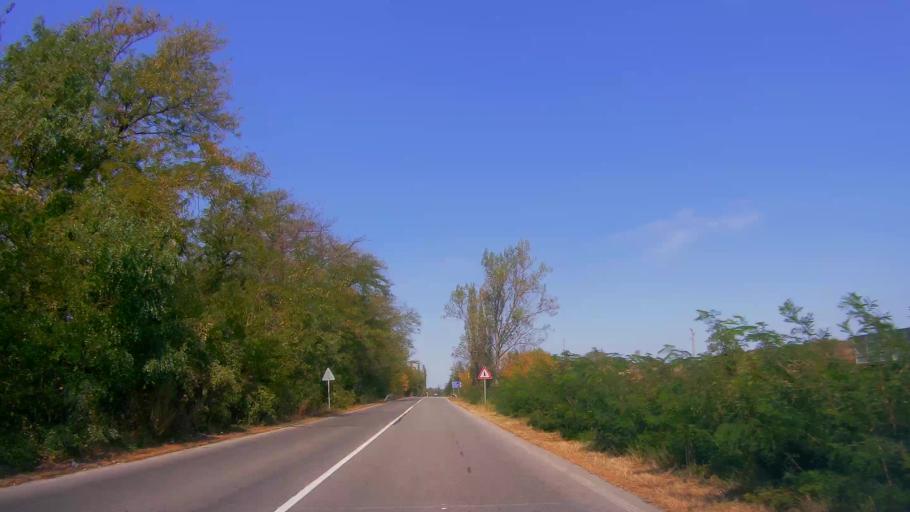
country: BG
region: Shumen
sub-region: Obshtina Smyadovo
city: Smyadovo
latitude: 43.1530
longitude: 27.0209
